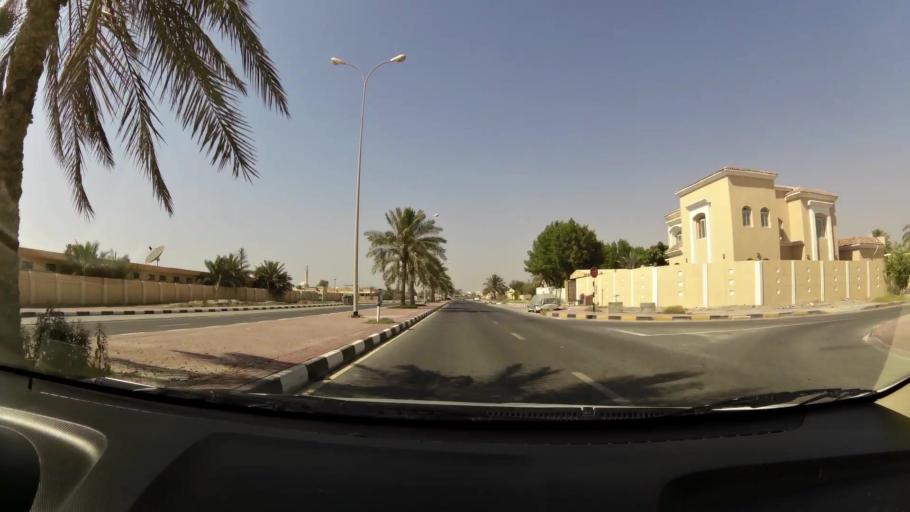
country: AE
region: Ajman
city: Ajman
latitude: 25.4118
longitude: 55.4710
